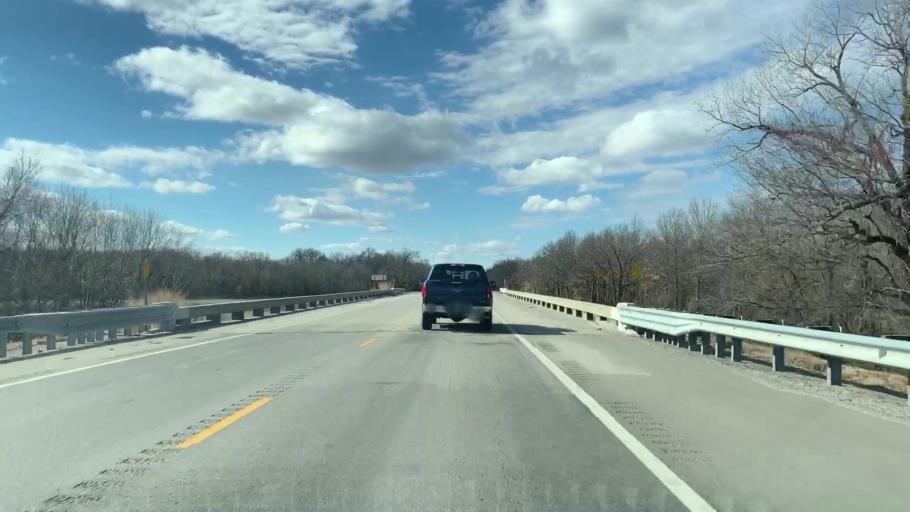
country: US
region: Kansas
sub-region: Cherokee County
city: Columbus
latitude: 37.3401
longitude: -94.9643
